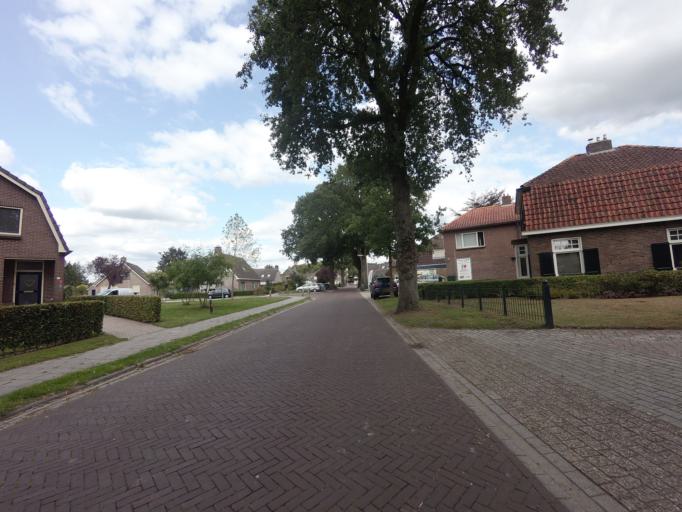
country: NL
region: Drenthe
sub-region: Gemeente De Wolden
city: Ruinen
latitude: 52.7617
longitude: 6.3584
